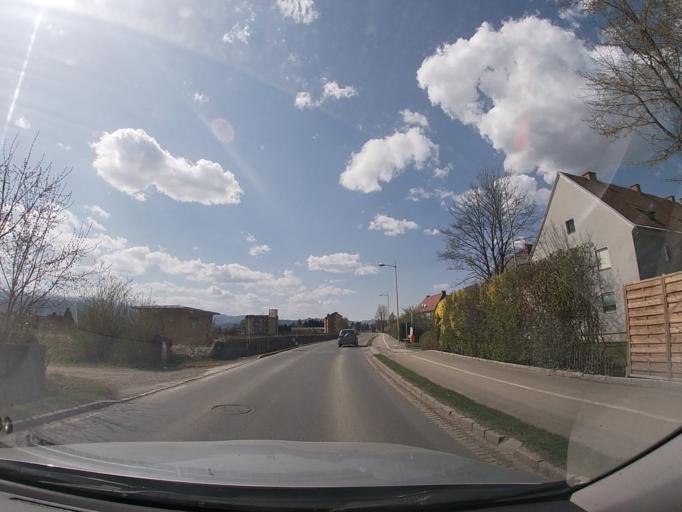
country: AT
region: Styria
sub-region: Politischer Bezirk Murtal
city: Zeltweg
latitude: 47.1902
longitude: 14.7404
